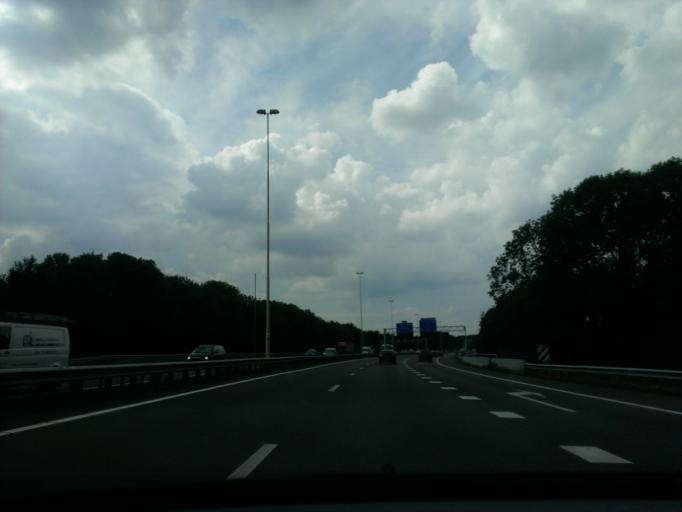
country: NL
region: Utrecht
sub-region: Gemeente Leusden
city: Leusden
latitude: 52.1677
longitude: 5.4474
